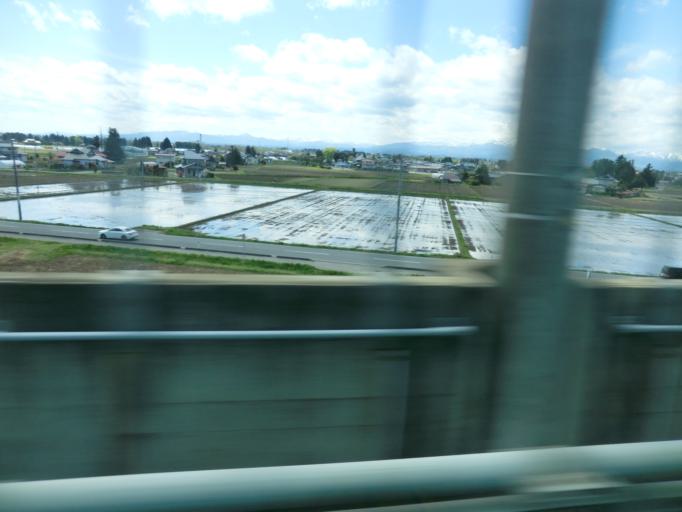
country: JP
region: Iwate
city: Mizusawa
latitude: 39.1715
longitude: 141.1786
